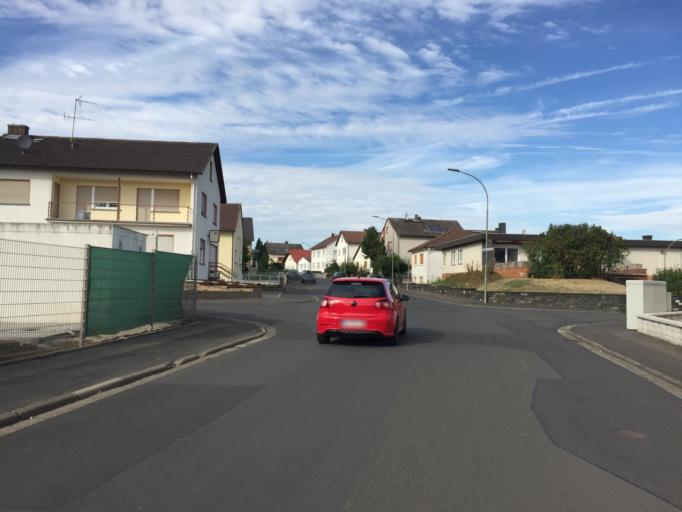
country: DE
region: Hesse
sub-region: Regierungsbezirk Darmstadt
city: Rockenberg
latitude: 50.4865
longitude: 8.7254
